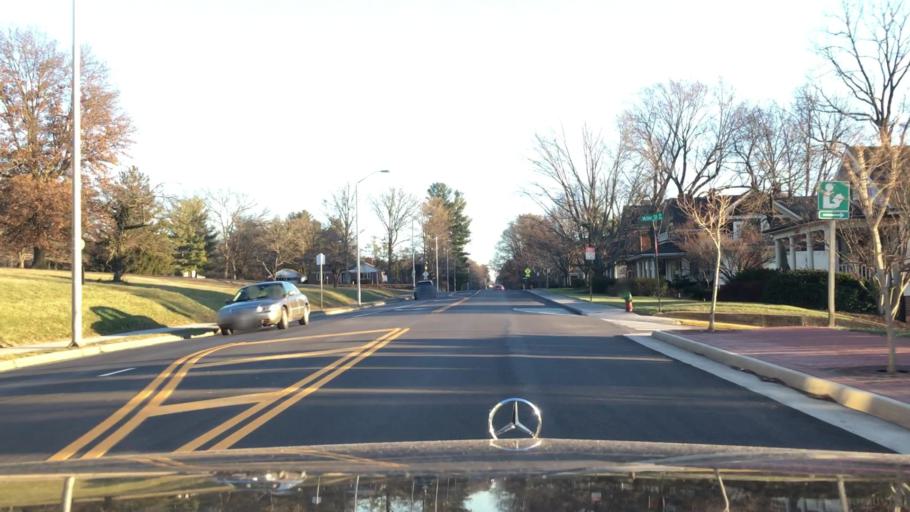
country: US
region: Virginia
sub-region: Montgomery County
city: Blacksburg
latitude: 37.2268
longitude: -80.4113
